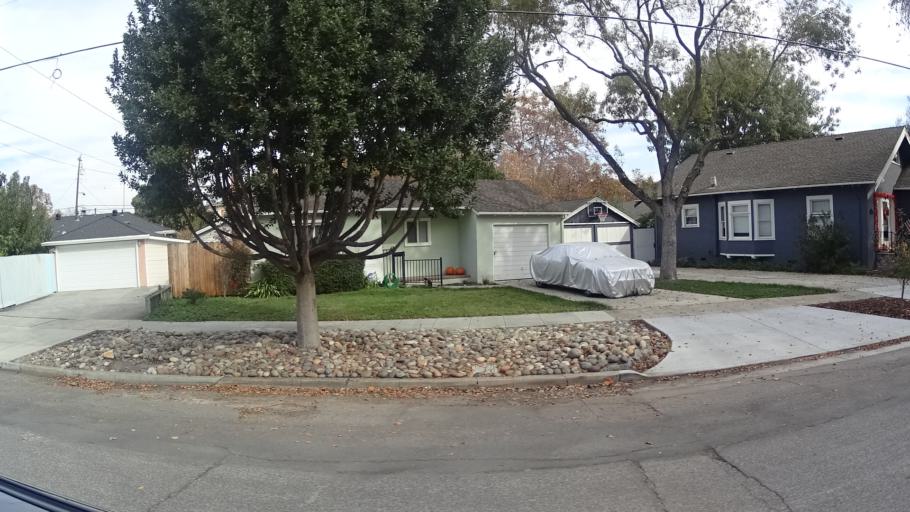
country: US
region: California
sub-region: Santa Clara County
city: Burbank
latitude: 37.3418
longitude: -121.9306
